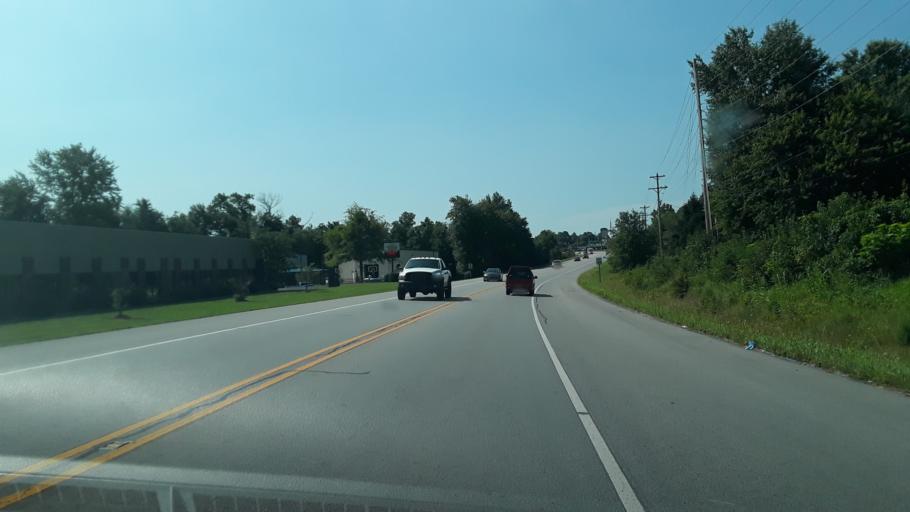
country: US
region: Indiana
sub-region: Clark County
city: Sellersburg
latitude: 38.3875
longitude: -85.7715
